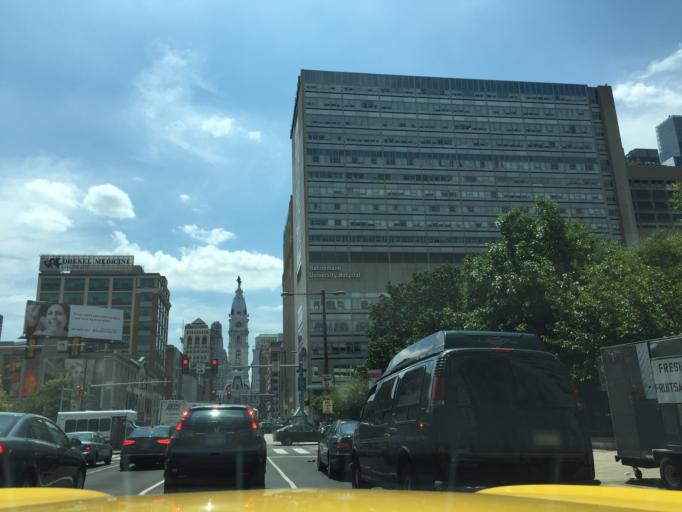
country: US
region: Pennsylvania
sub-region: Philadelphia County
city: Philadelphia
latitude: 39.9585
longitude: -75.1624
